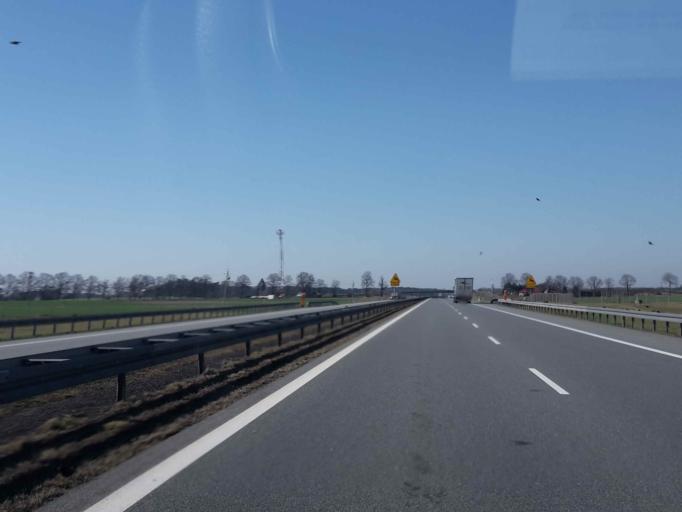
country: PL
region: Greater Poland Voivodeship
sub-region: Powiat nowotomyski
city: Lwowek
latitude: 52.3721
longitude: 16.2197
